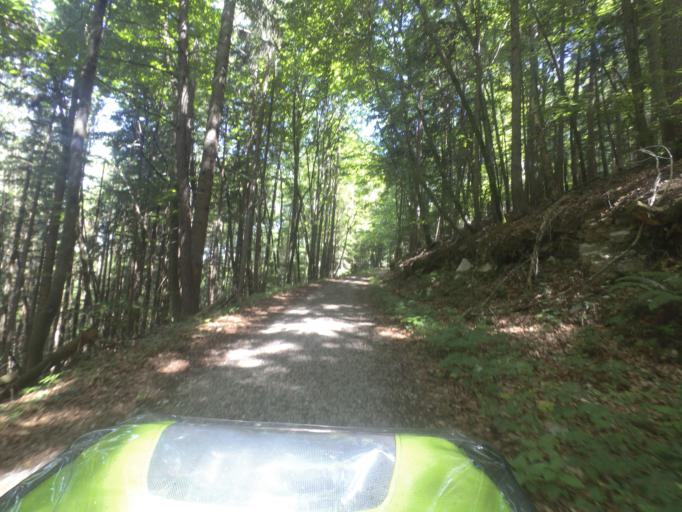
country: AT
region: Salzburg
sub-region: Politischer Bezirk Hallein
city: Puch bei Hallein
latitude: 47.7145
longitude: 13.1102
